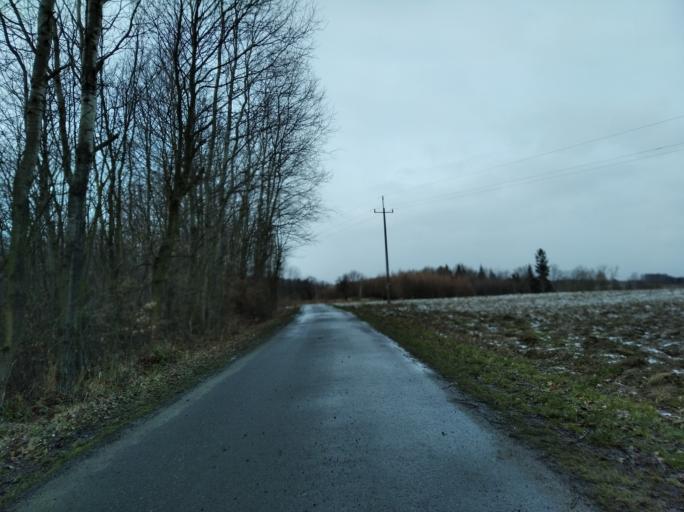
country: PL
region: Subcarpathian Voivodeship
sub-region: Powiat strzyzowski
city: Strzyzow
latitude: 49.8958
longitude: 21.7345
